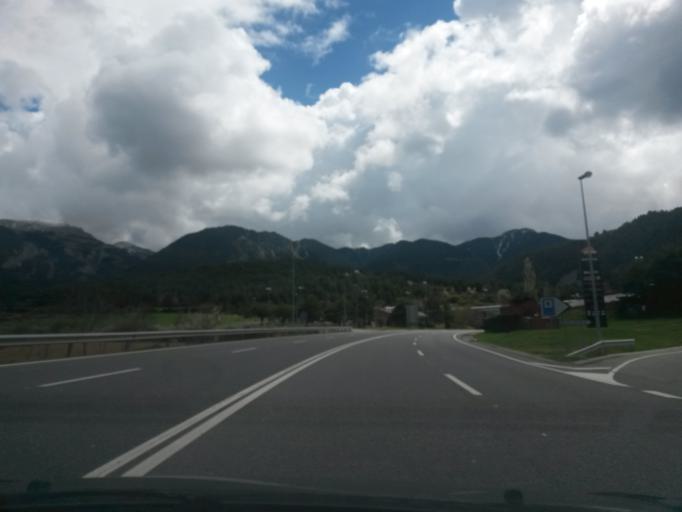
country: ES
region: Catalonia
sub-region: Provincia de Lleida
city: Riu de Cerdanya
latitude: 42.3477
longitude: 1.8328
